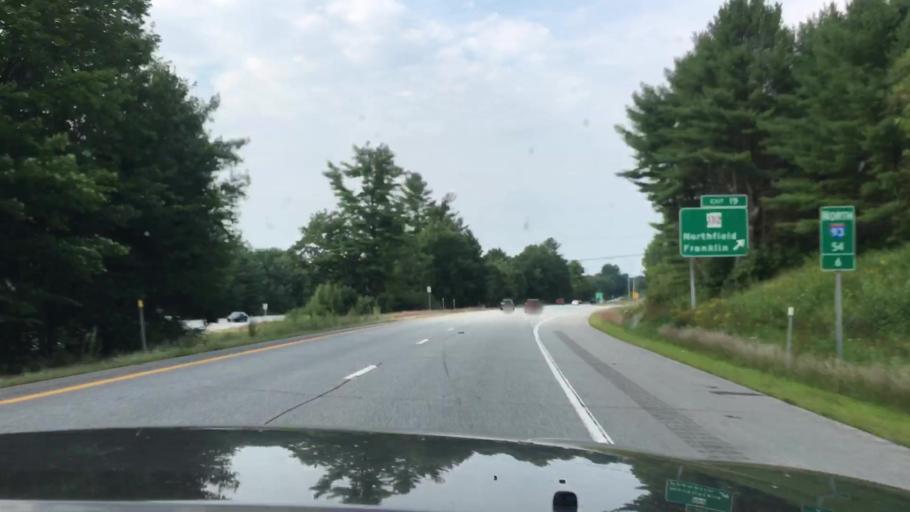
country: US
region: New Hampshire
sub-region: Merrimack County
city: Northfield
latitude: 43.4250
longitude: -71.5910
